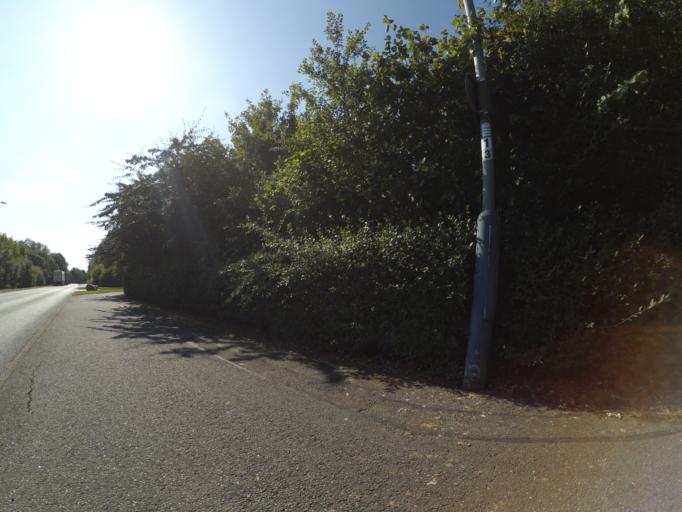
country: GB
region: England
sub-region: Warwickshire
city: Rugby
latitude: 52.3966
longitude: -1.2641
